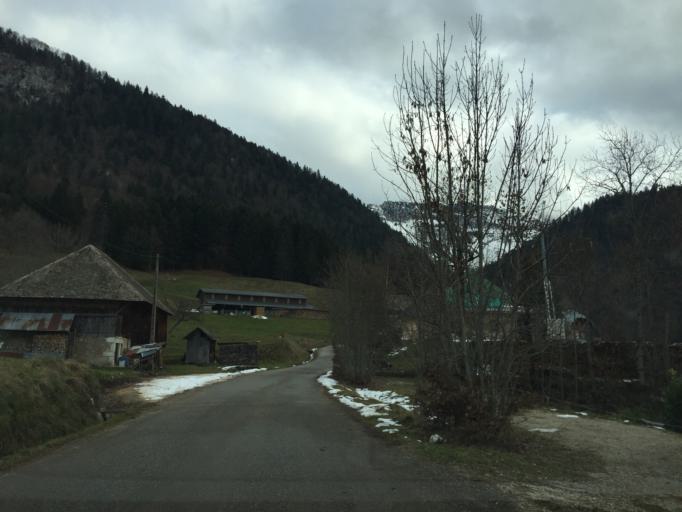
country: FR
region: Rhone-Alpes
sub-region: Departement de la Haute-Savoie
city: Doussard
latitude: 45.7347
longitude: 6.1630
